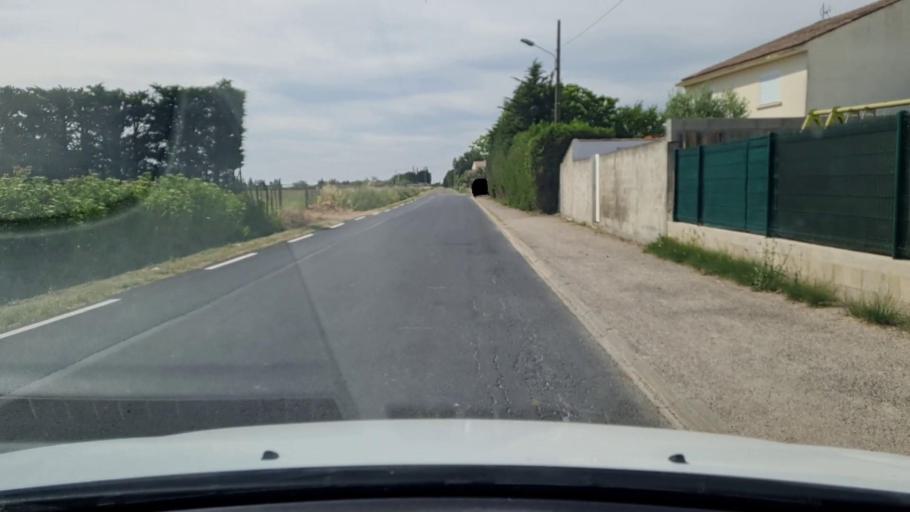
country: FR
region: Languedoc-Roussillon
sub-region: Departement de l'Herault
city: Marsillargues
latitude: 43.6300
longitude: 4.1965
